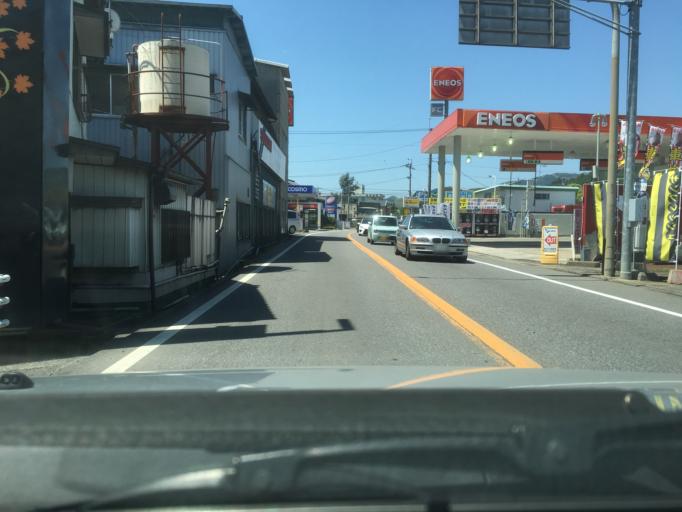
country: JP
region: Oita
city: Beppu
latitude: 33.2666
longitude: 131.3606
